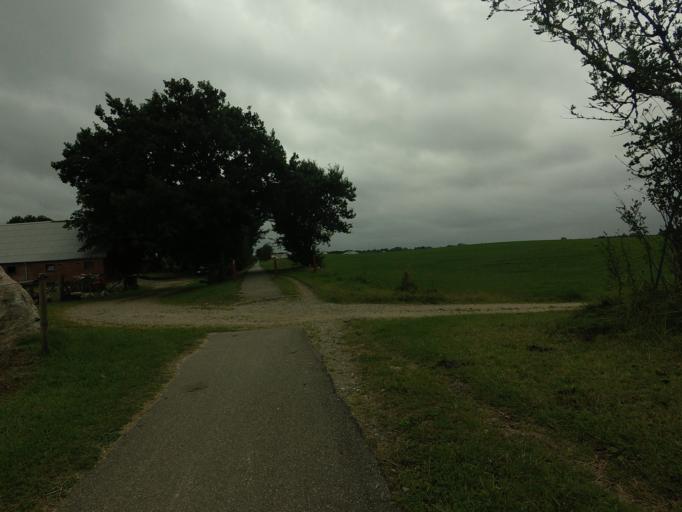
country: DK
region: Central Jutland
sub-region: Horsens Kommune
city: Braedstrup
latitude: 55.9901
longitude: 9.5898
